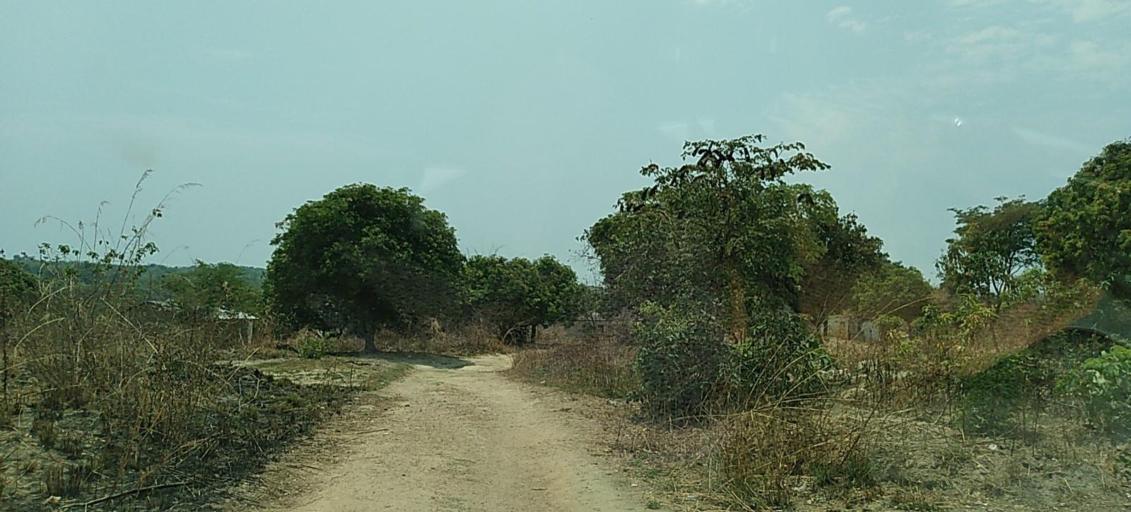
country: ZM
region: Copperbelt
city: Kalulushi
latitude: -12.9563
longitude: 28.1456
